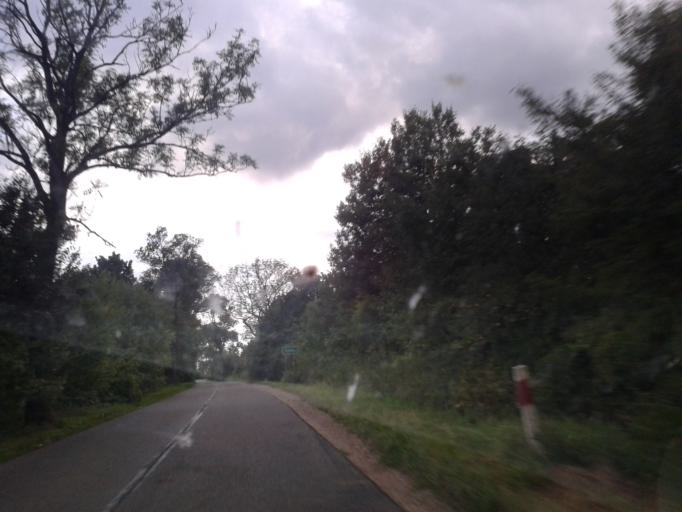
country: PL
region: West Pomeranian Voivodeship
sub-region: Powiat koszalinski
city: Bobolice
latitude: 53.8971
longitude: 16.5266
